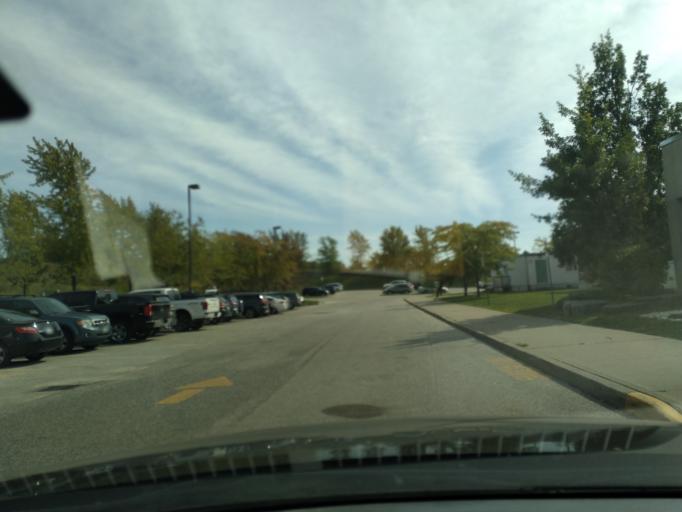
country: CA
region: Ontario
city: Keswick
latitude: 44.2126
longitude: -79.4602
